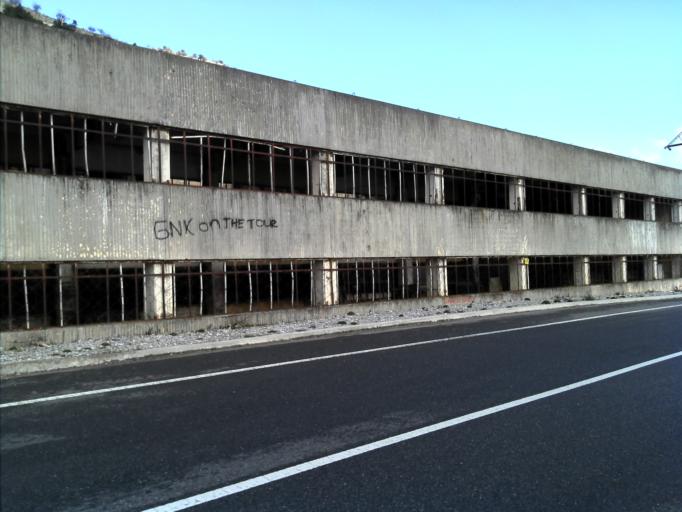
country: AL
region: Shkoder
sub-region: Rrethi i Malesia e Madhe
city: Hot
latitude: 42.3340
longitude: 19.4266
